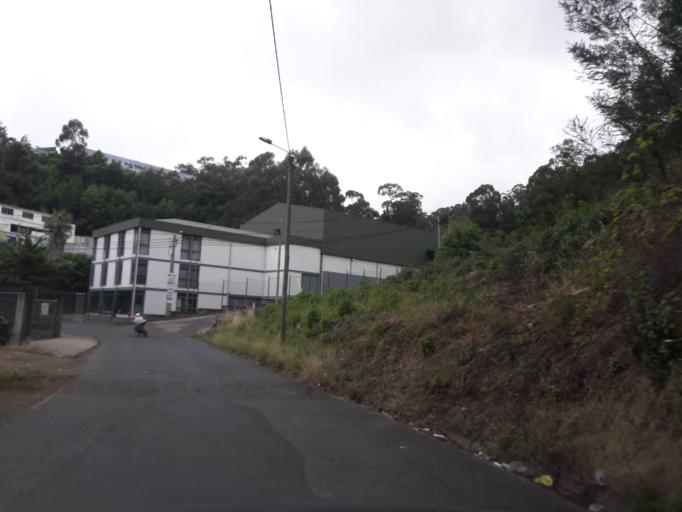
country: PT
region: Madeira
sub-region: Santa Cruz
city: Camacha
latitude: 32.6595
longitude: -16.8577
